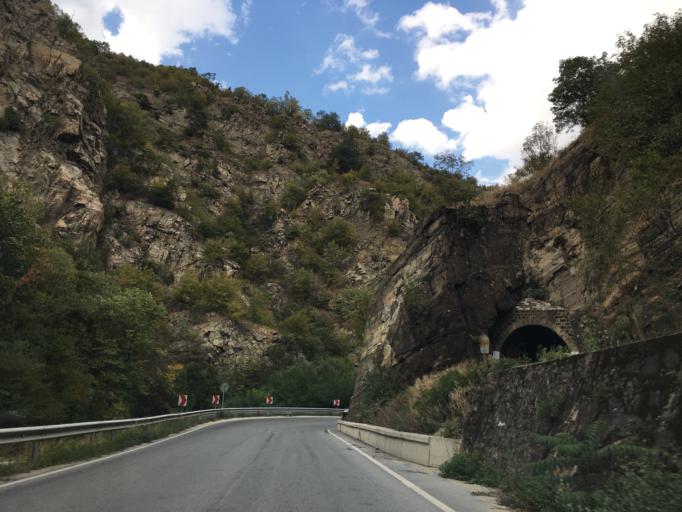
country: BG
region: Pazardzhik
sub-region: Obshtina Septemvri
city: Septemvri
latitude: 42.1223
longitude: 24.1203
